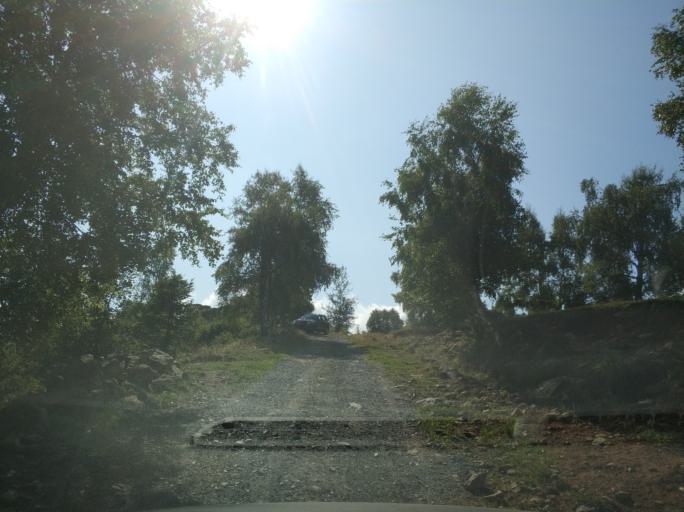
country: IT
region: Piedmont
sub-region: Provincia di Torino
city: Viu
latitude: 45.1969
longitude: 7.3616
